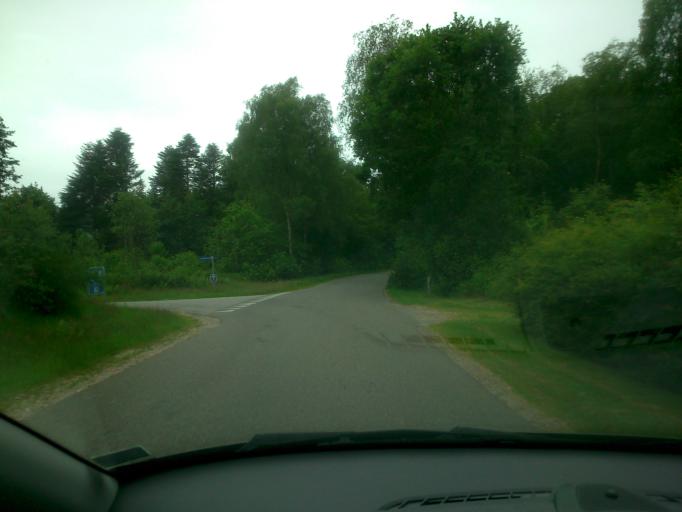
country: DK
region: Central Jutland
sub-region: Ringkobing-Skjern Kommune
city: Skjern
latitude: 56.0005
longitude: 8.4640
